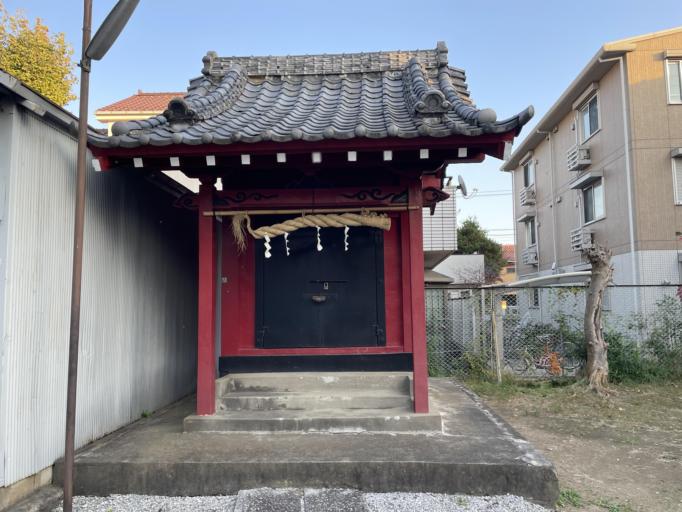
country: JP
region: Chiba
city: Matsudo
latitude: 35.7427
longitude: 139.8377
